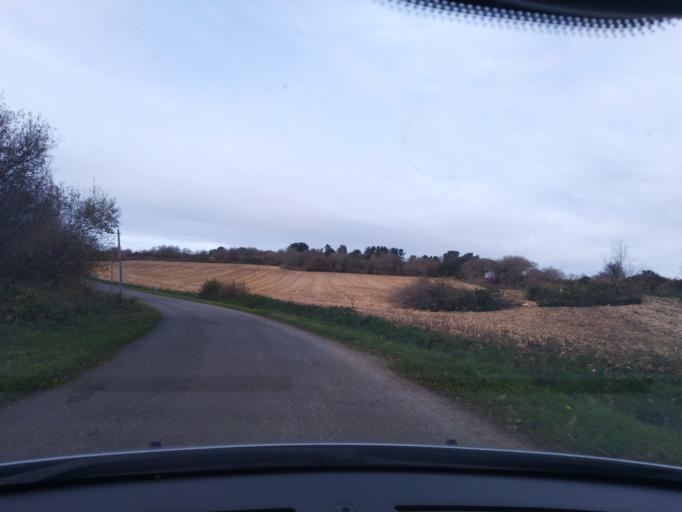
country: FR
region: Brittany
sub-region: Departement du Finistere
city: Guerlesquin
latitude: 48.5215
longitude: -3.5964
